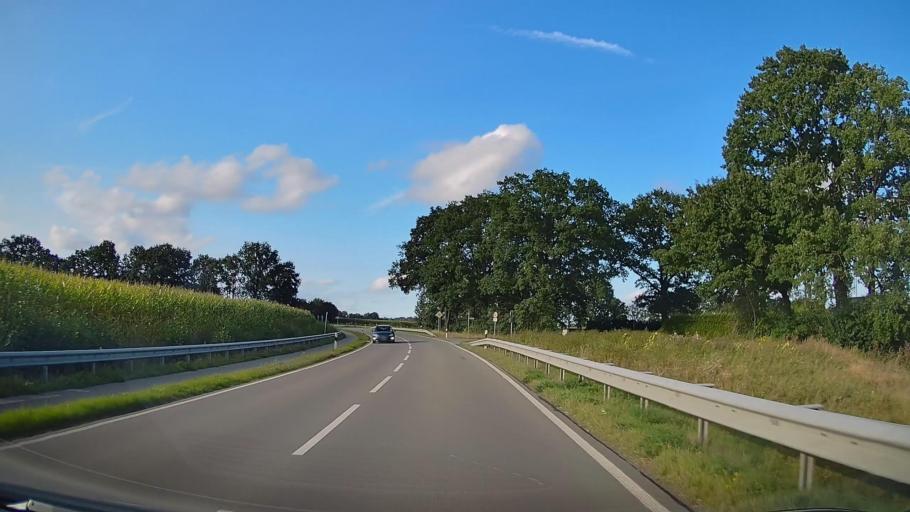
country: DE
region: Lower Saxony
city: Hilkenbrook
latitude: 53.0669
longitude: 7.7225
